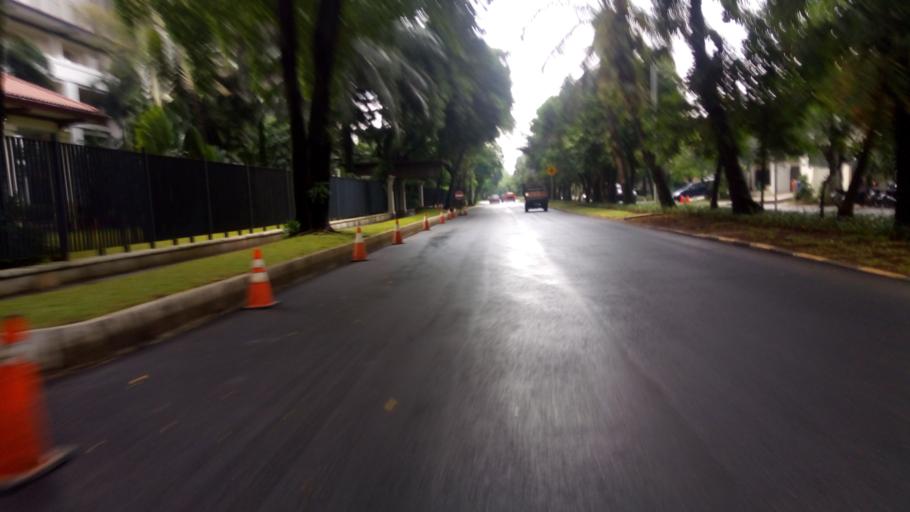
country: ID
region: Jakarta Raya
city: Jakarta
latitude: -6.2537
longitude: 106.8054
